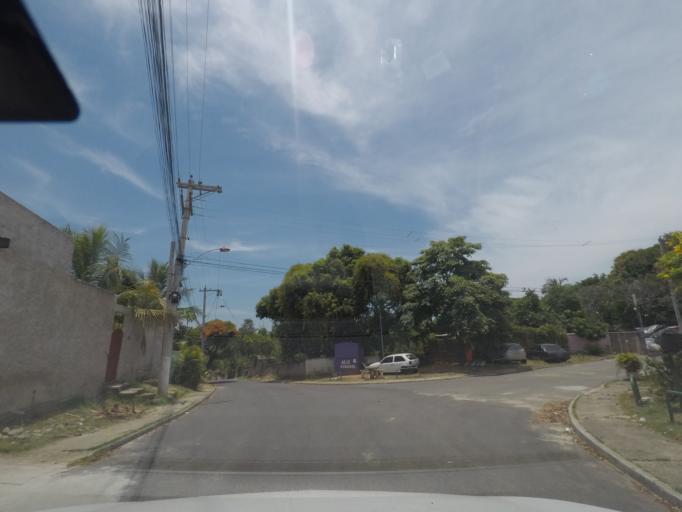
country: BR
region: Rio de Janeiro
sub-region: Marica
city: Marica
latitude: -22.9333
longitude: -42.8265
